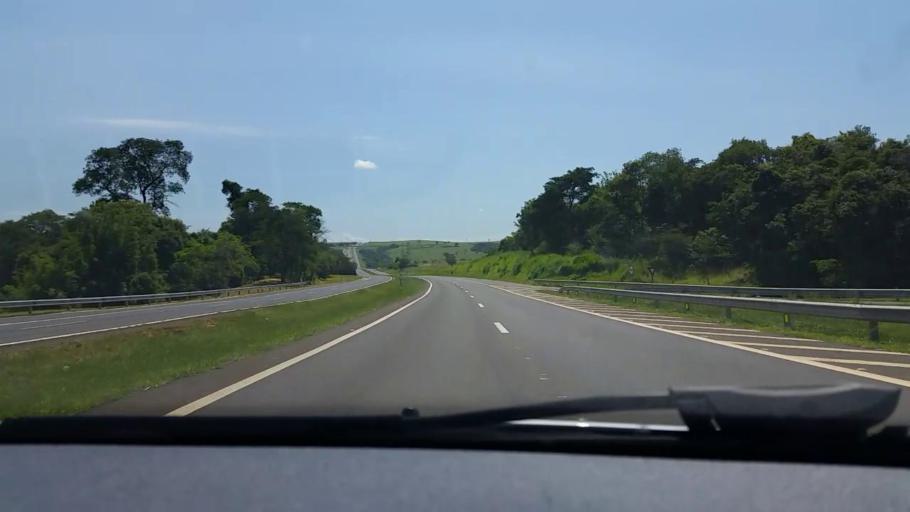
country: BR
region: Sao Paulo
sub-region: Bauru
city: Bauru
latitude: -22.4164
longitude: -49.1090
